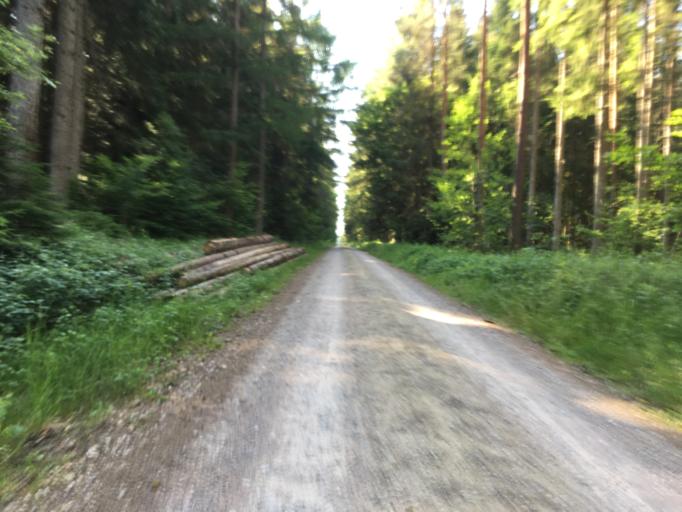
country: DE
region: Baden-Wuerttemberg
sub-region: Freiburg Region
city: Loffingen
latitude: 47.9276
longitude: 8.3504
